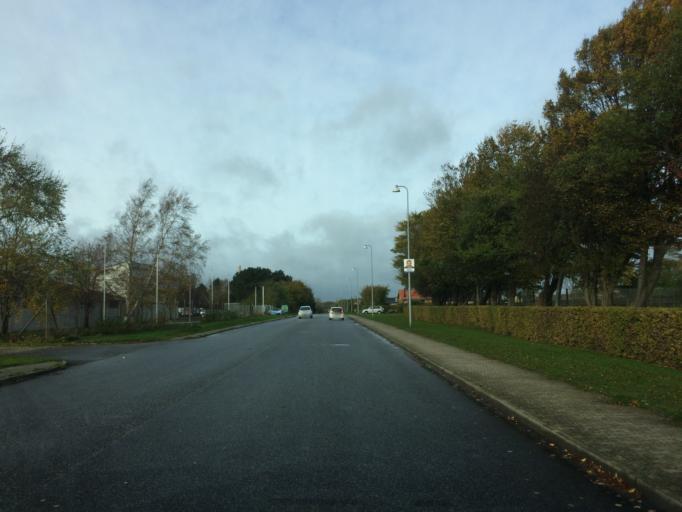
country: DK
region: South Denmark
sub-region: Fredericia Kommune
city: Fredericia
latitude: 55.5779
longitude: 9.7459
